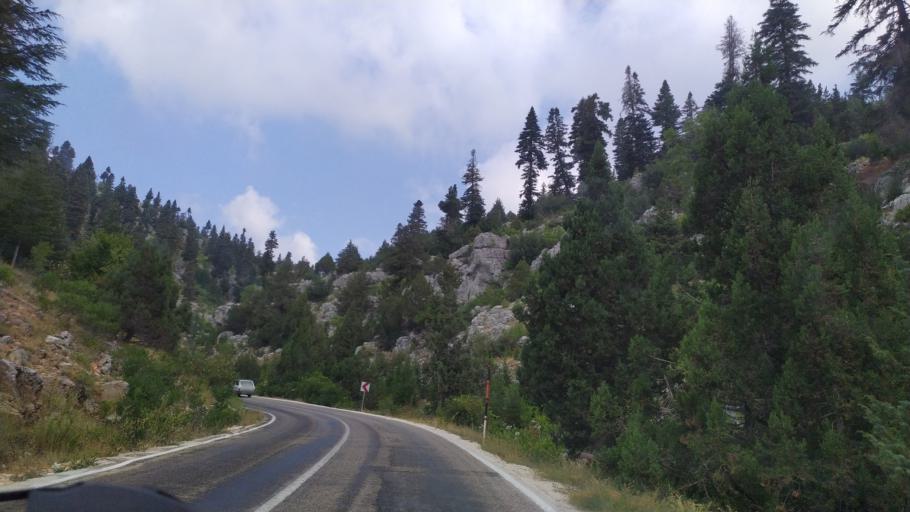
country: TR
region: Mersin
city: Kirobasi
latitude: 36.6064
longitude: 33.8856
